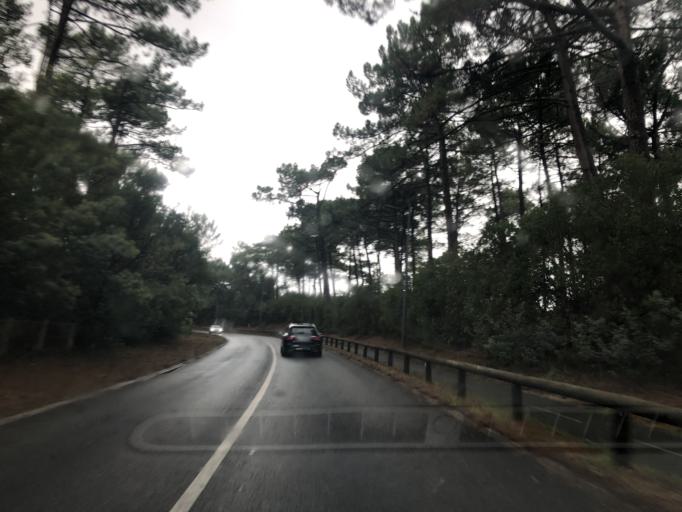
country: FR
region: Aquitaine
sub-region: Departement de la Gironde
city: Arcachon
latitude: 44.6926
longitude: -1.2381
